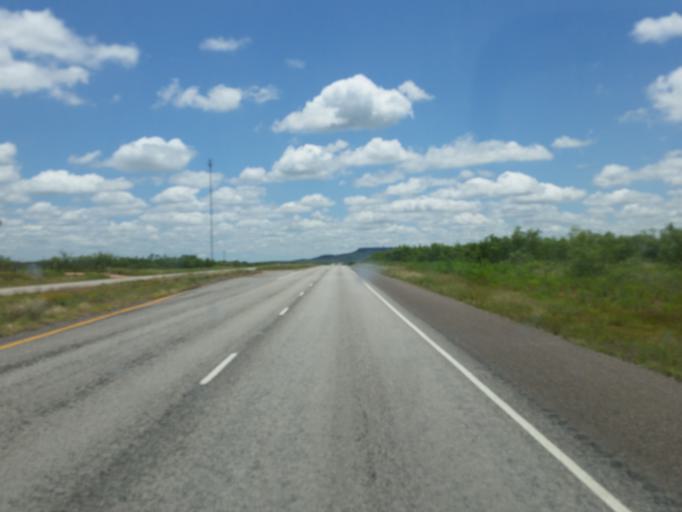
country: US
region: Texas
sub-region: Garza County
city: Post
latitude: 32.9869
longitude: -101.1336
